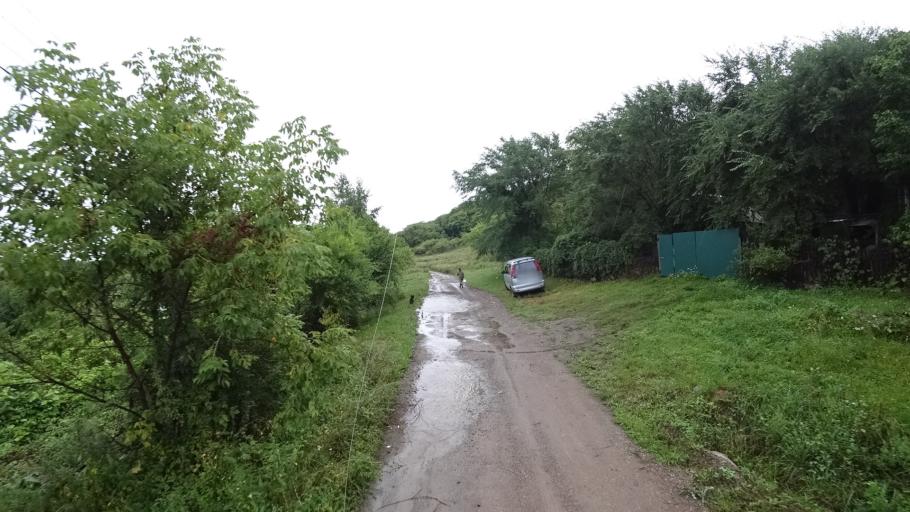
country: RU
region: Primorskiy
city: Monastyrishche
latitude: 44.2656
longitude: 132.4041
